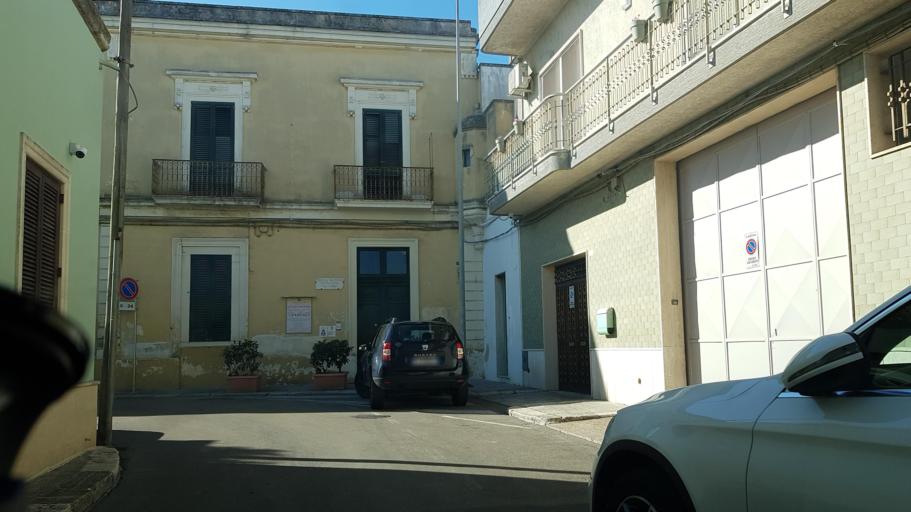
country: IT
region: Apulia
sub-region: Provincia di Lecce
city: Arnesano
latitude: 40.3364
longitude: 18.0907
